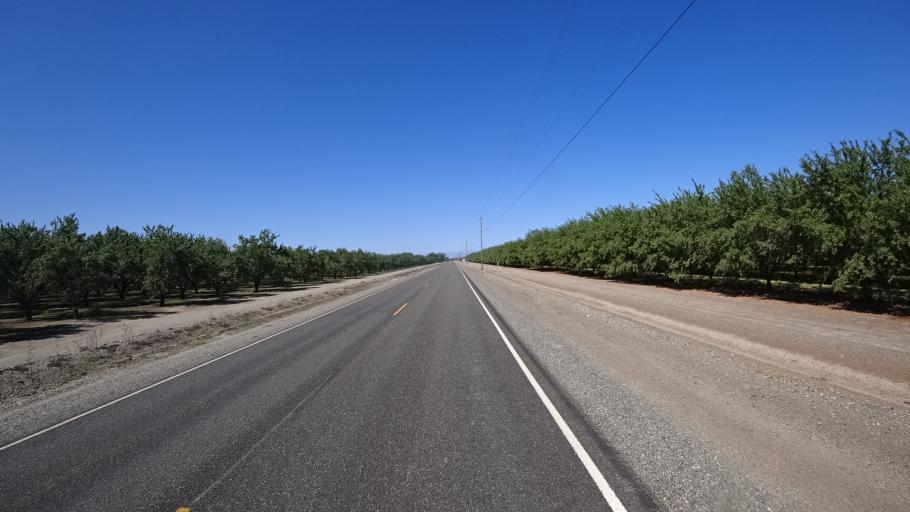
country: US
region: California
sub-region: Glenn County
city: Hamilton City
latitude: 39.7106
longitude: -122.0903
